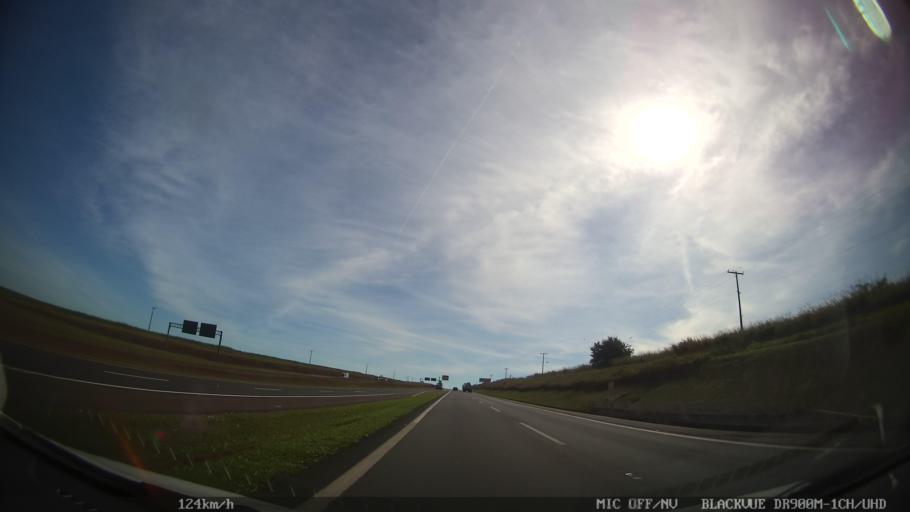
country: BR
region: Sao Paulo
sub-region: Cordeiropolis
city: Cordeiropolis
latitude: -22.4781
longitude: -47.3989
